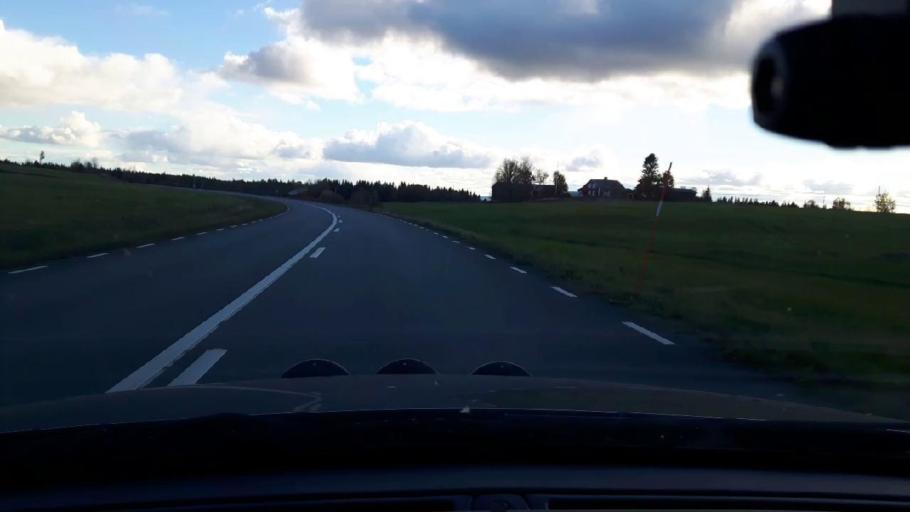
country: SE
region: Jaemtland
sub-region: Krokoms Kommun
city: Krokom
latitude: 63.0792
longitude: 14.2913
